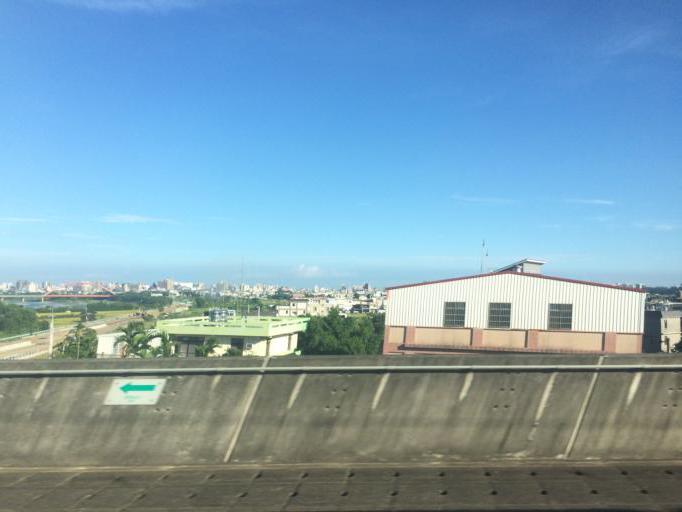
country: TW
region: Taiwan
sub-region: Hsinchu
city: Hsinchu
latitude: 24.6822
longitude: 120.9304
